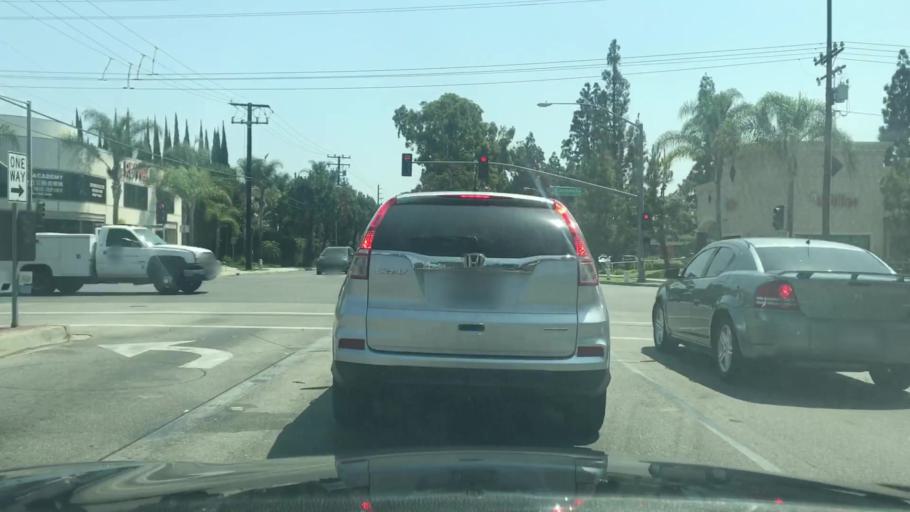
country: US
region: California
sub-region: Orange County
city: Anaheim
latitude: 33.8243
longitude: -117.9456
